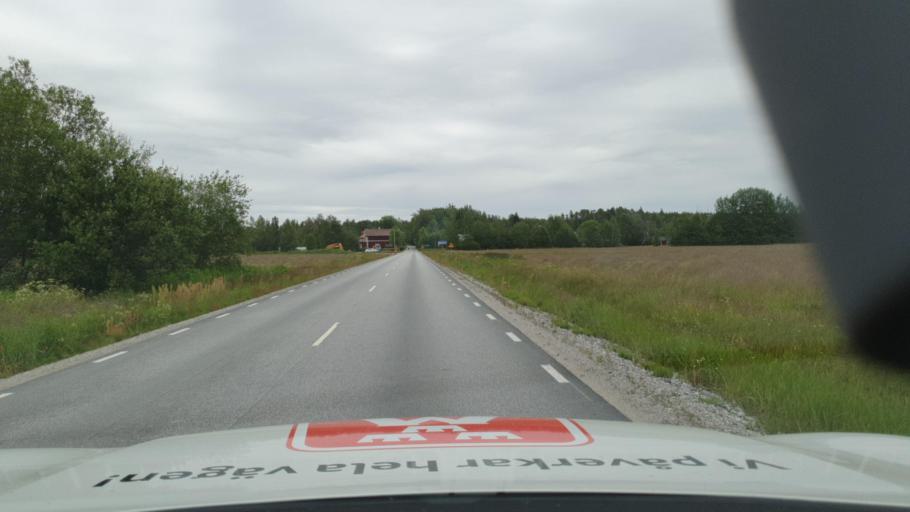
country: SE
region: Vaesterbotten
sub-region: Nordmalings Kommun
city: Nordmaling
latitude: 63.5786
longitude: 19.4372
